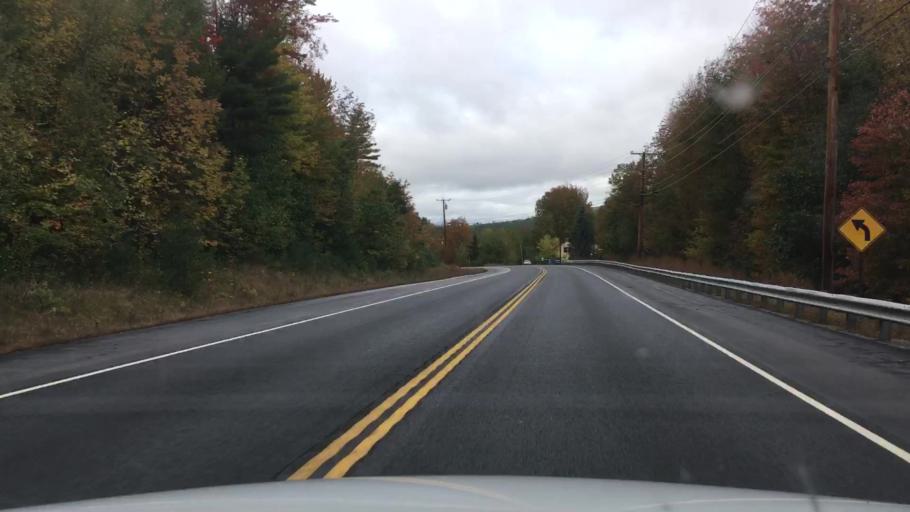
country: US
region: Maine
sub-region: Oxford County
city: Bethel
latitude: 44.4163
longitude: -70.8363
